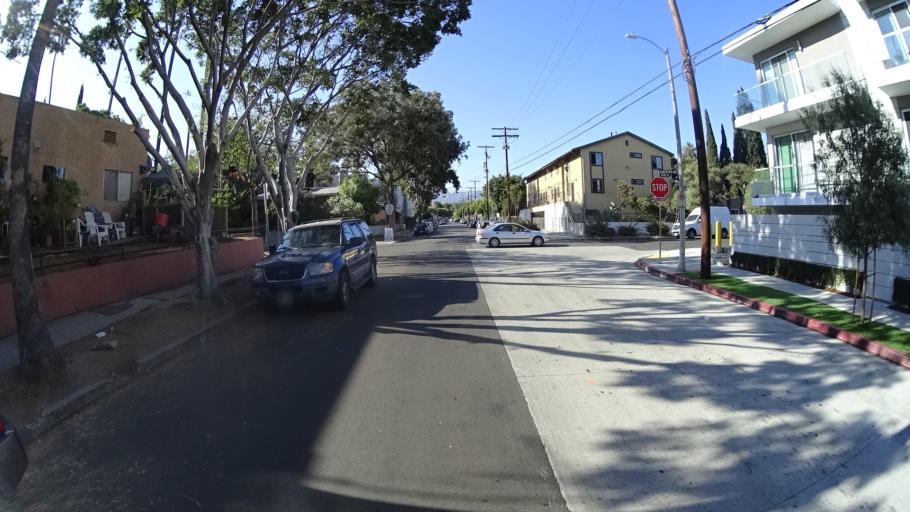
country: US
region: California
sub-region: Los Angeles County
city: Hollywood
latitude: 34.0842
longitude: -118.3244
